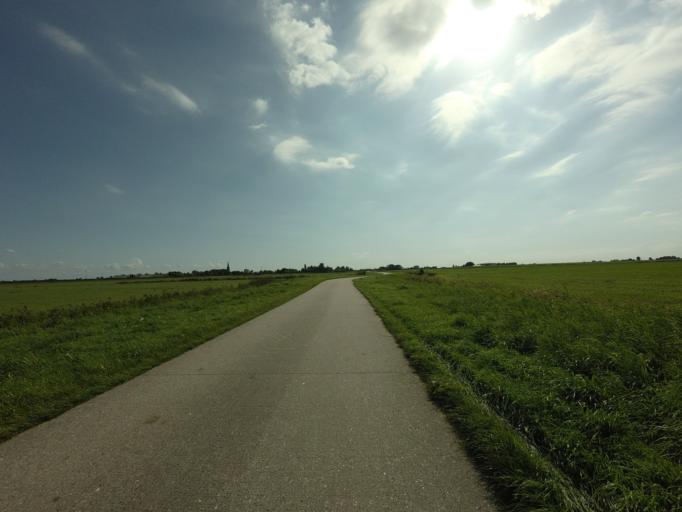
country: NL
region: Friesland
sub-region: Gemeente Littenseradiel
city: Makkum
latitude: 53.0833
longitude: 5.6321
